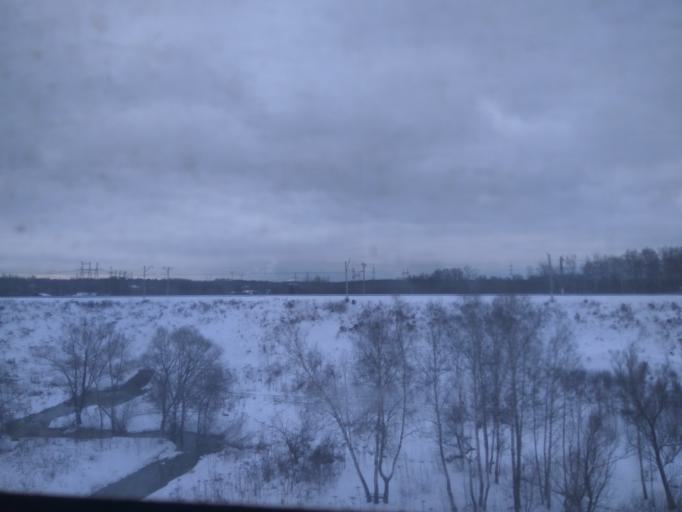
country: RU
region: Moscow
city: Annino
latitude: 55.5671
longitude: 37.6076
